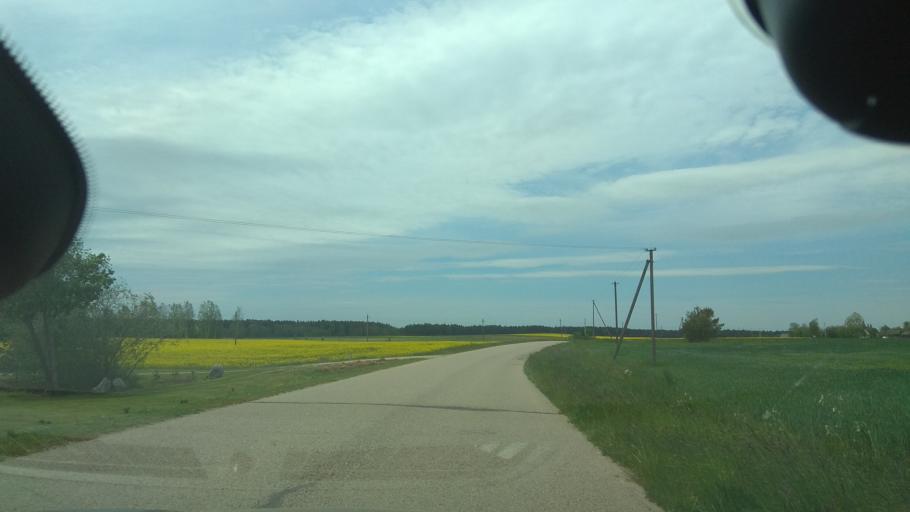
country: LT
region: Vilnius County
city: Ukmerge
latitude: 55.1609
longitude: 24.5272
